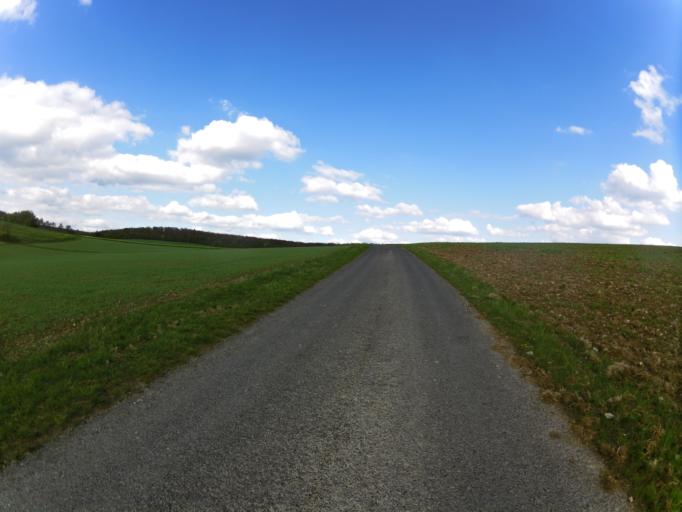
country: DE
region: Bavaria
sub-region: Regierungsbezirk Unterfranken
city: Greussenheim
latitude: 49.7818
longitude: 9.7755
